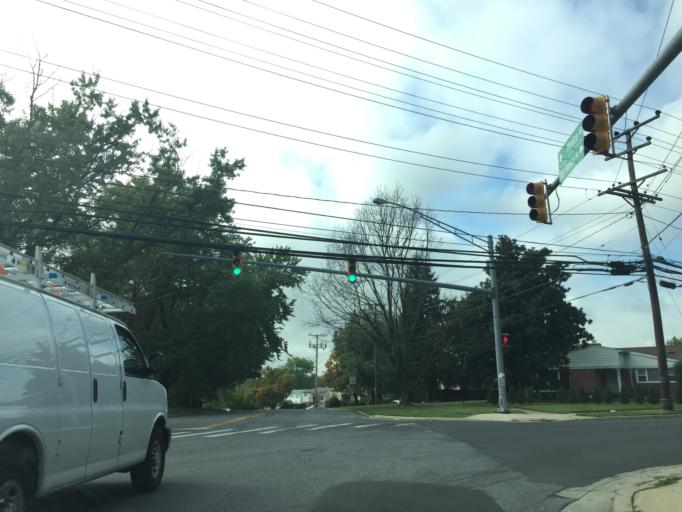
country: US
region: Maryland
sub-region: Baltimore County
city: Pikesville
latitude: 39.3753
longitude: -76.6779
